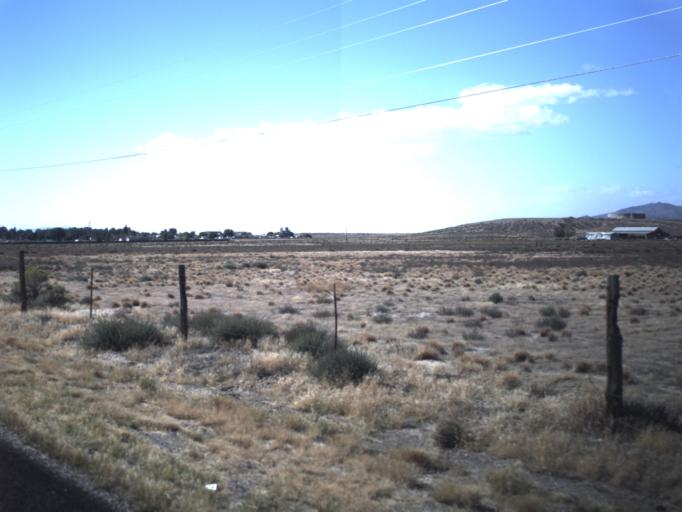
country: US
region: Utah
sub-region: Beaver County
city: Milford
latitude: 38.4113
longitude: -113.0099
